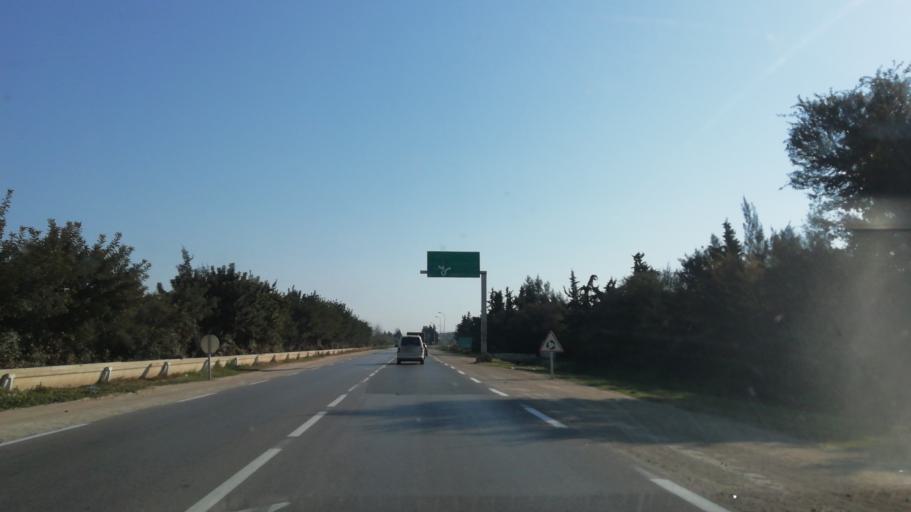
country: DZ
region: Relizane
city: Relizane
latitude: 35.7222
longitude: 0.5034
